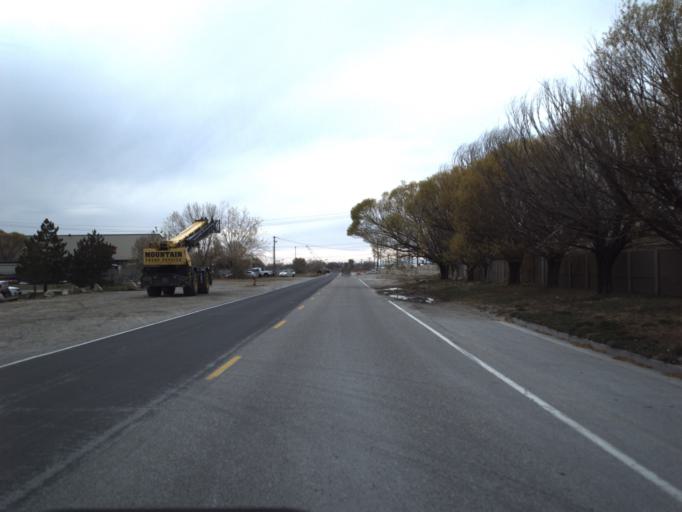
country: US
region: Utah
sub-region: Davis County
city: North Salt Lake
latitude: 40.8168
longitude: -111.9241
